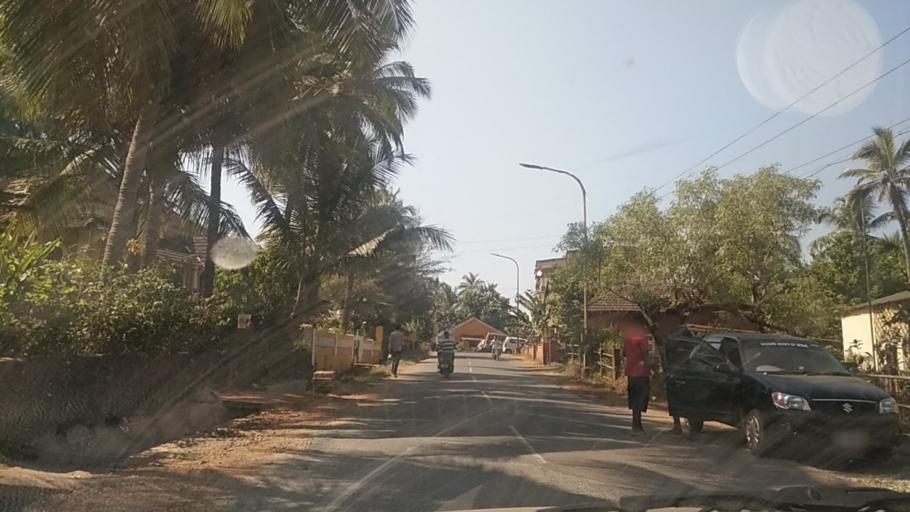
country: IN
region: Goa
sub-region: South Goa
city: Raia
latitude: 15.2976
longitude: 73.9595
